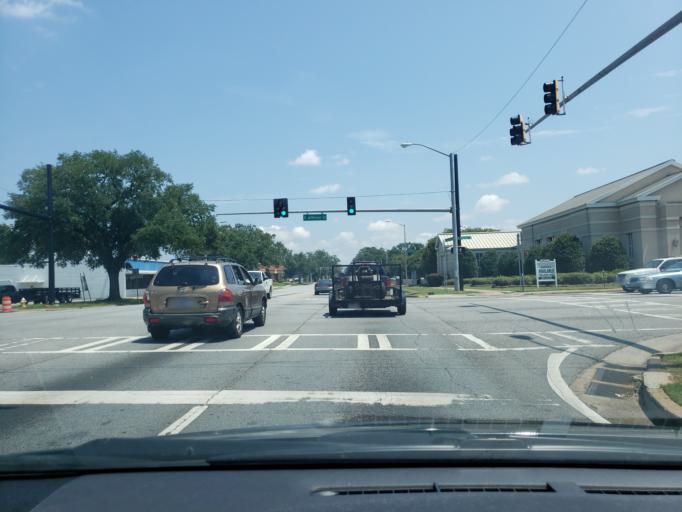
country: US
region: Georgia
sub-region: Dougherty County
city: Albany
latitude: 31.5753
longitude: -84.1562
